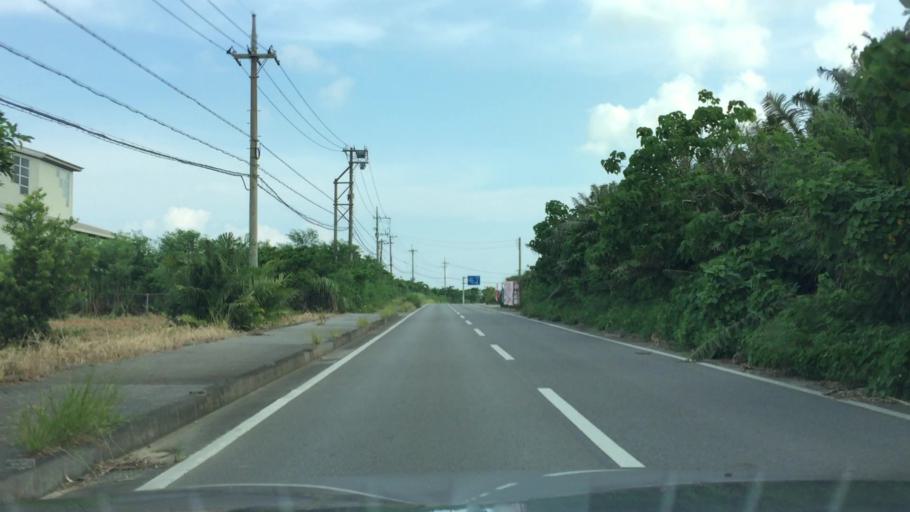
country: JP
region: Okinawa
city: Ishigaki
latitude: 24.3964
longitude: 124.1952
